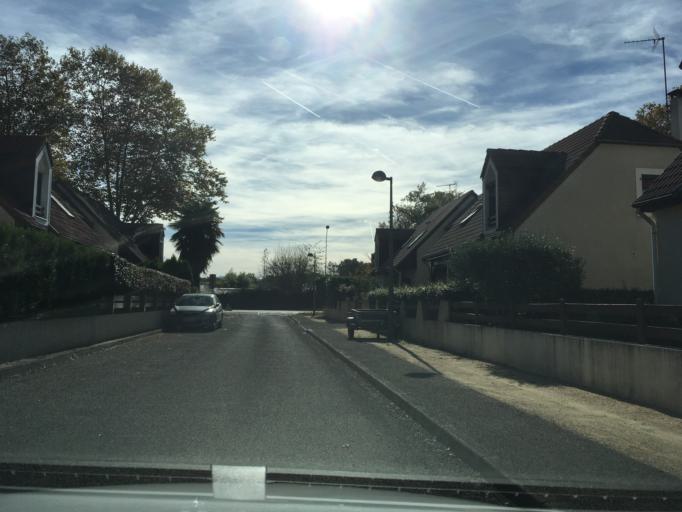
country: FR
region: Aquitaine
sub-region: Departement des Pyrenees-Atlantiques
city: Pau
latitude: 43.3296
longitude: -0.3520
